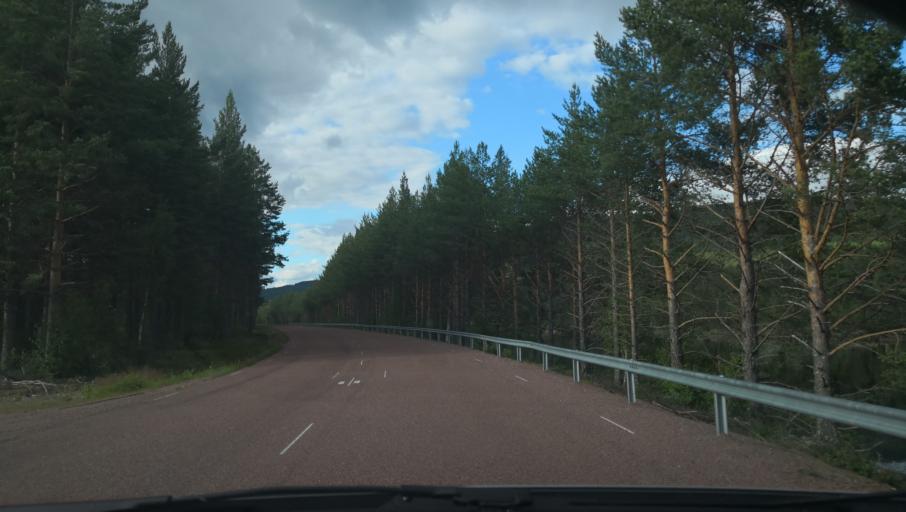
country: SE
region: Dalarna
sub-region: Alvdalens Kommun
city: AElvdalen
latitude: 61.3159
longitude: 13.7324
